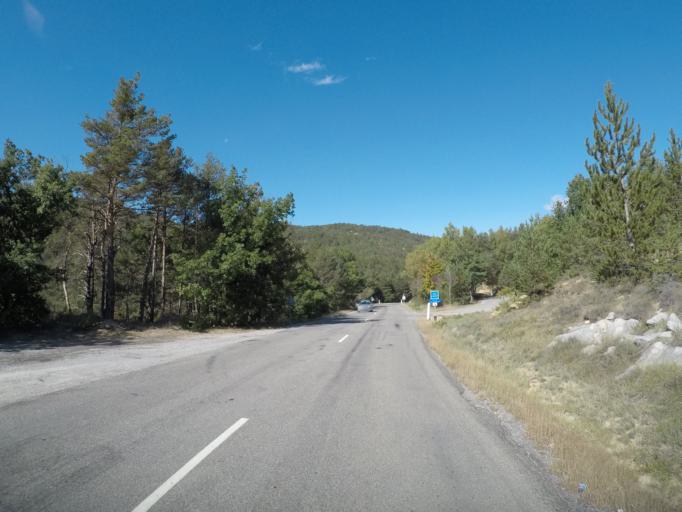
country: FR
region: Provence-Alpes-Cote d'Azur
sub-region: Departement des Alpes-de-Haute-Provence
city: Mallemoisson
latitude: 44.0247
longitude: 6.1723
